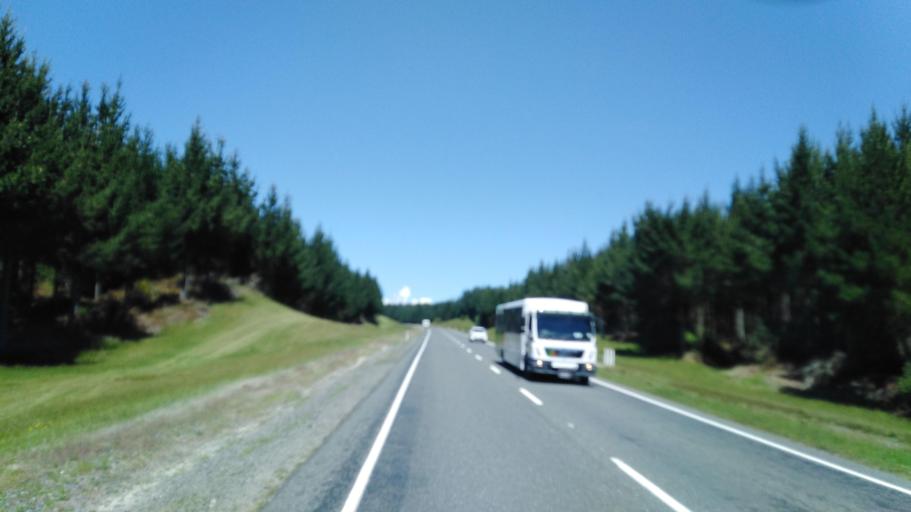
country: NZ
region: Waikato
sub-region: Taupo District
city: Taupo
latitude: -38.8233
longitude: 176.0716
